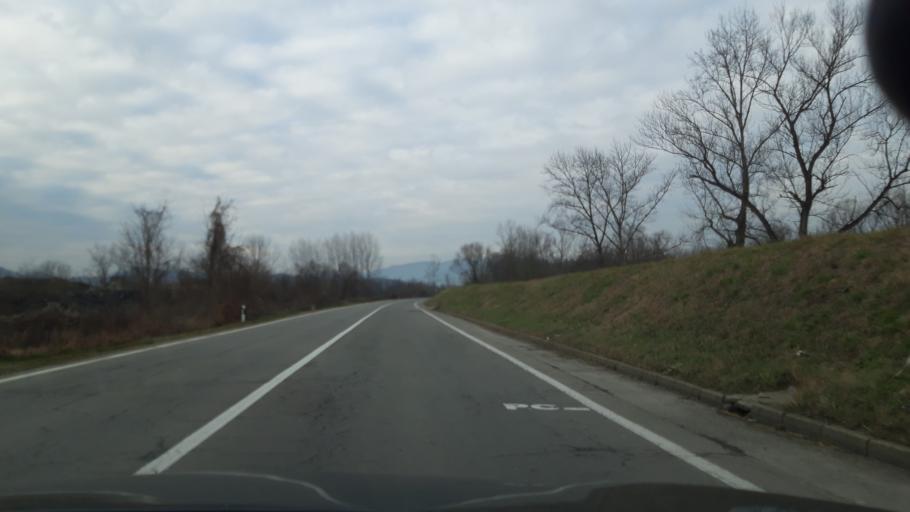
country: BA
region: Republika Srpska
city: Petkovci
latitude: 44.5197
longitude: 19.1643
